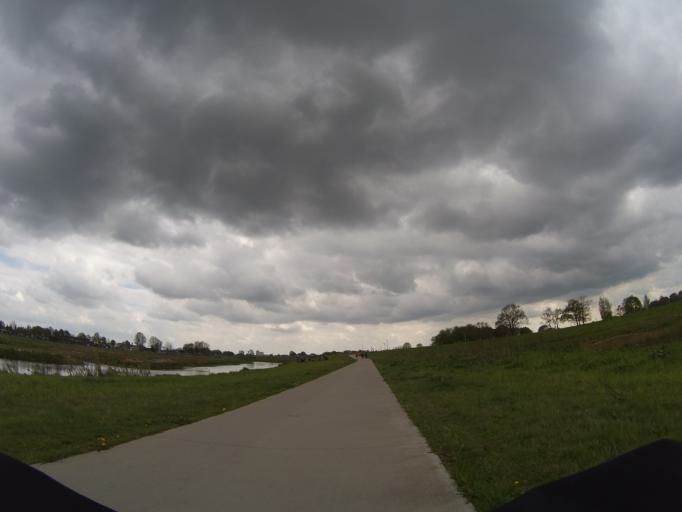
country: NL
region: Overijssel
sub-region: Gemeente Hardenberg
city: Hardenberg
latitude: 52.5682
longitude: 6.6122
